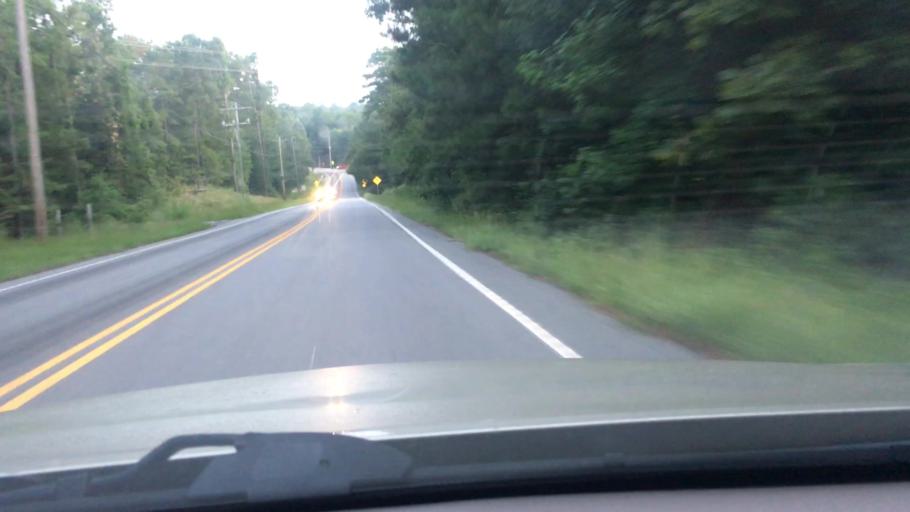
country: US
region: South Carolina
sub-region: Lexington County
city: Irmo
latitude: 34.1451
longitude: -81.1930
